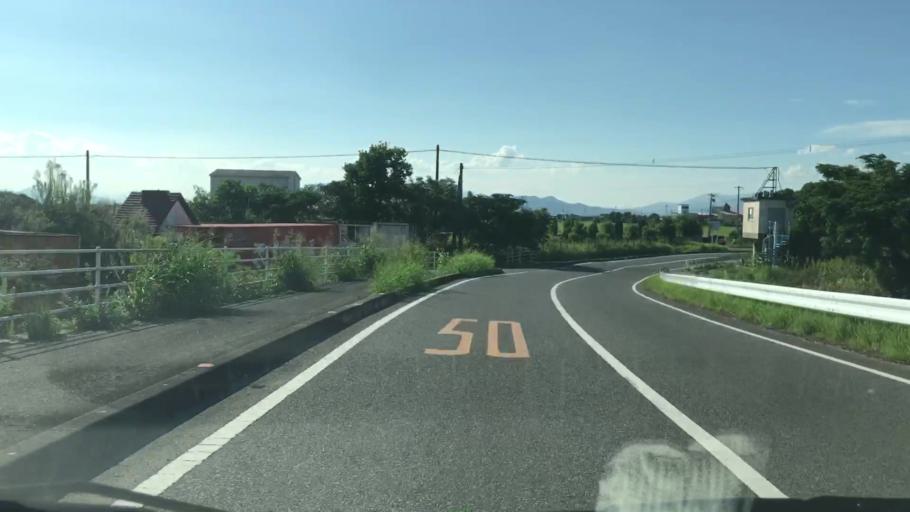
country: JP
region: Saga Prefecture
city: Okawa
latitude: 33.1864
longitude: 130.2907
